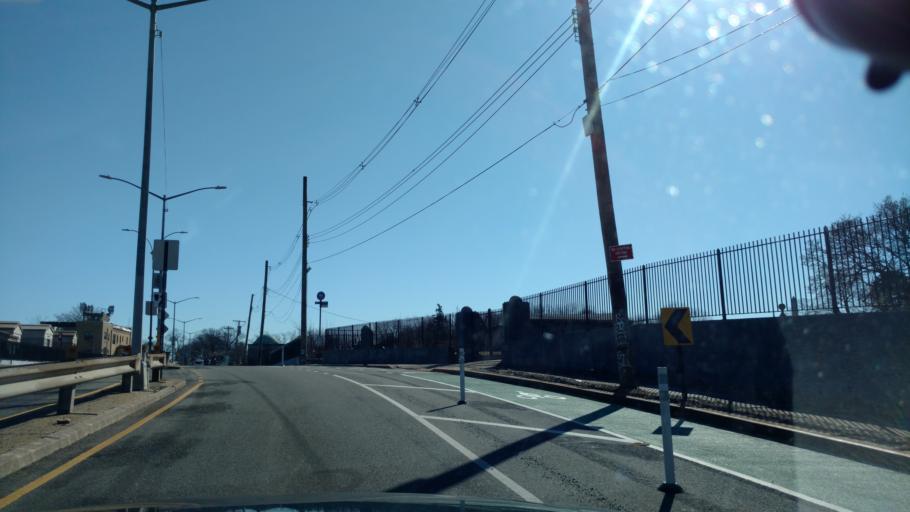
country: US
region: New York
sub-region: Kings County
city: East New York
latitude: 40.6940
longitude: -73.8847
